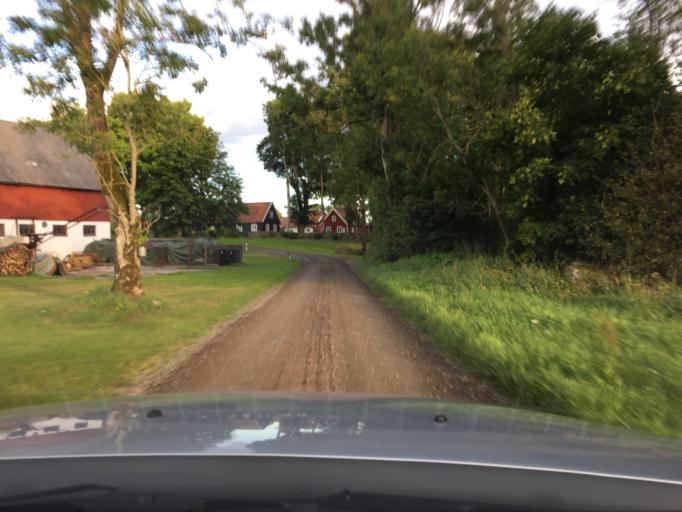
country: SE
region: Skane
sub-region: Hassleholms Kommun
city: Sosdala
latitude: 56.0317
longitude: 13.7156
